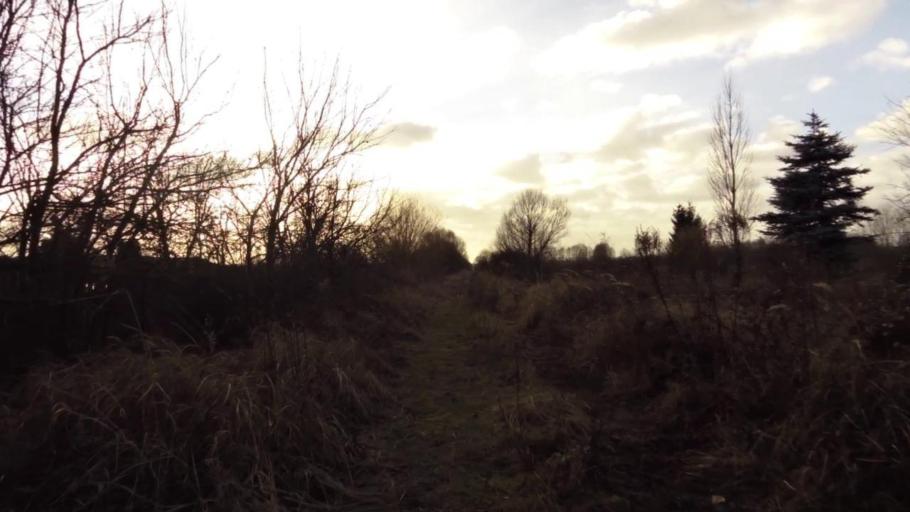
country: PL
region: West Pomeranian Voivodeship
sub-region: Powiat mysliborski
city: Mysliborz
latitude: 52.9164
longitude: 14.8526
